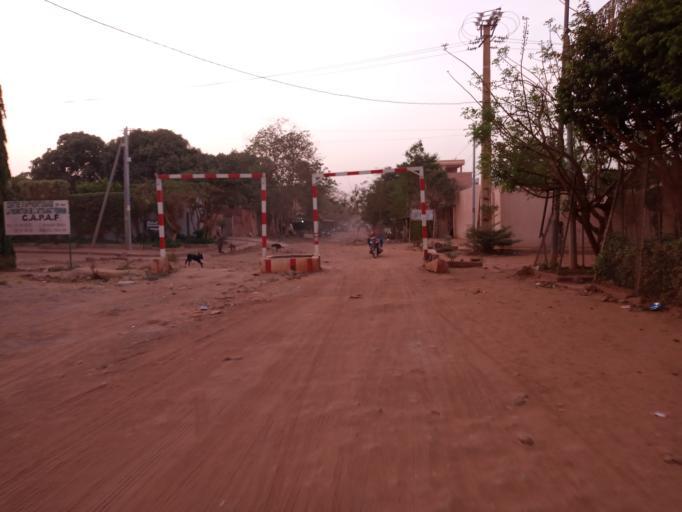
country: ML
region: Bamako
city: Bamako
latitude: 12.5845
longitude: -7.9504
